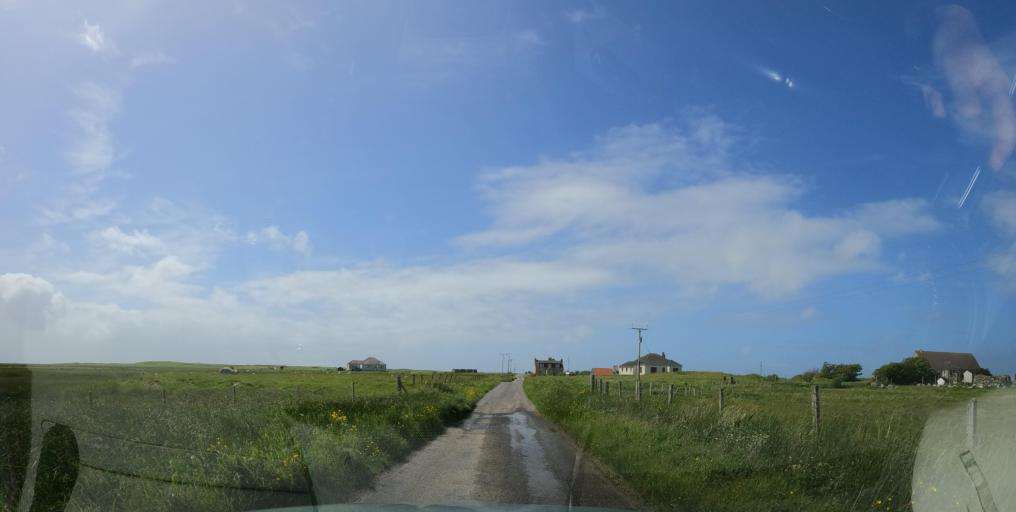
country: GB
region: Scotland
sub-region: Eilean Siar
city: Isle of South Uist
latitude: 57.1638
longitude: -7.3892
